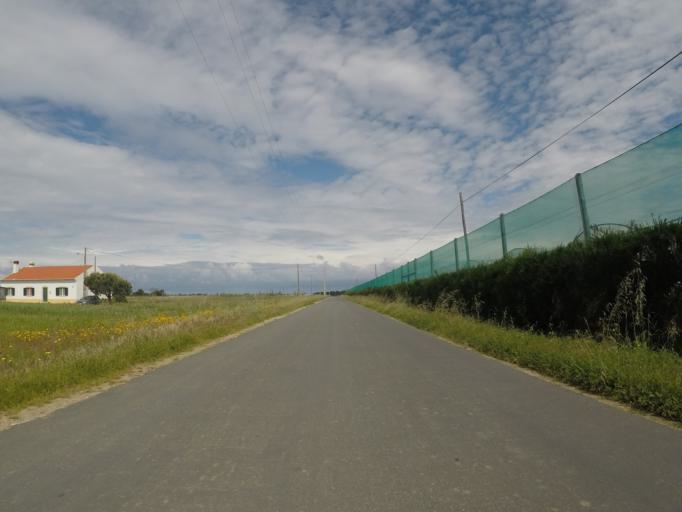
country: PT
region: Beja
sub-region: Odemira
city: Sao Teotonio
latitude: 37.4851
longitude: -8.7717
